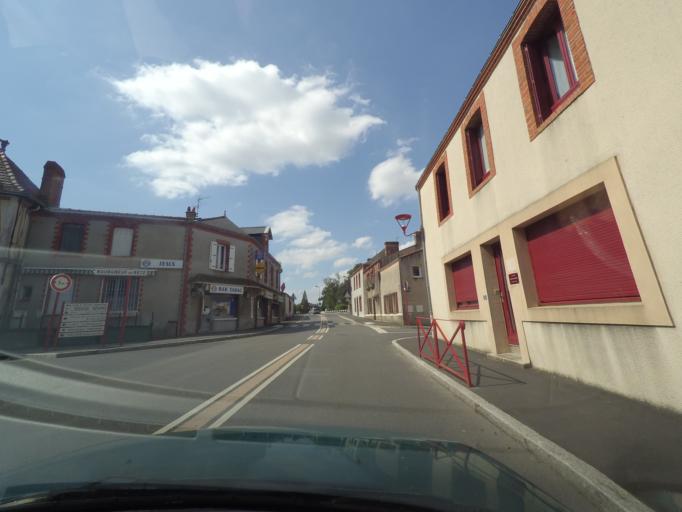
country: FR
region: Pays de la Loire
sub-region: Departement de la Loire-Atlantique
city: Saint-Hilaire-de-Chaleons
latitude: 47.1034
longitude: -1.8649
